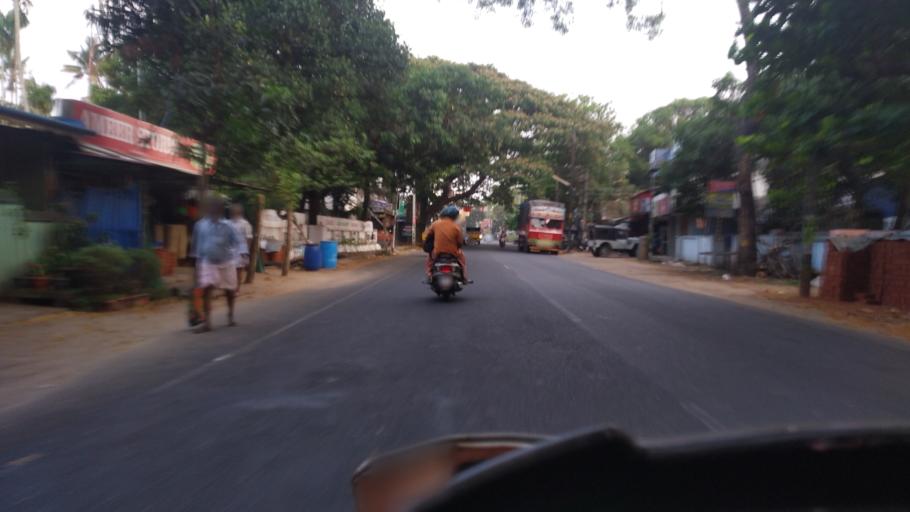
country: IN
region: Kerala
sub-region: Thrissur District
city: Kodungallur
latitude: 10.2452
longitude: 76.1898
